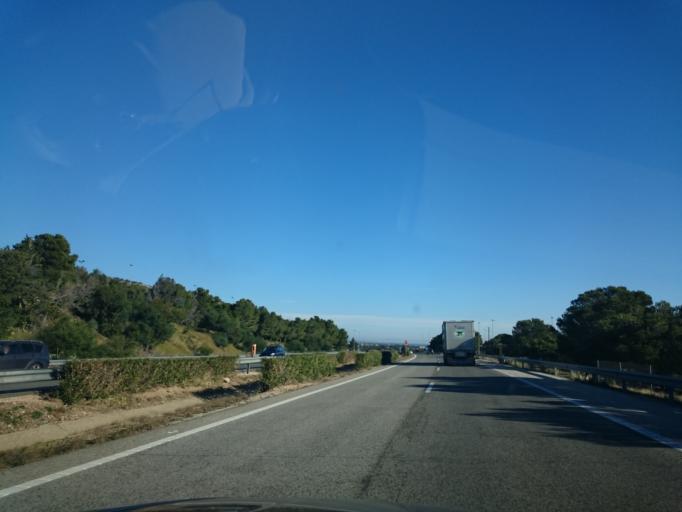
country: ES
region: Catalonia
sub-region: Provincia de Tarragona
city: Colldejou
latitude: 40.9853
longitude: 0.8955
